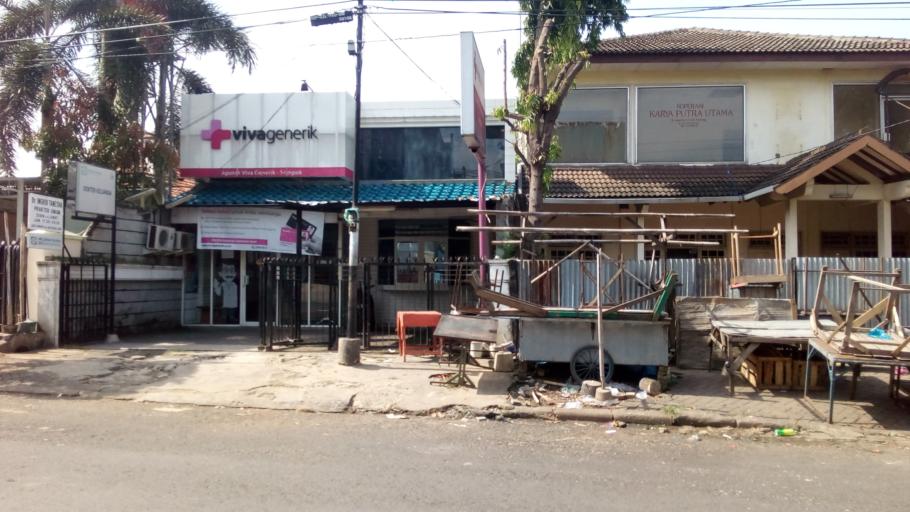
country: ID
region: Central Java
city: Semarang
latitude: -7.0051
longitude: 110.4337
